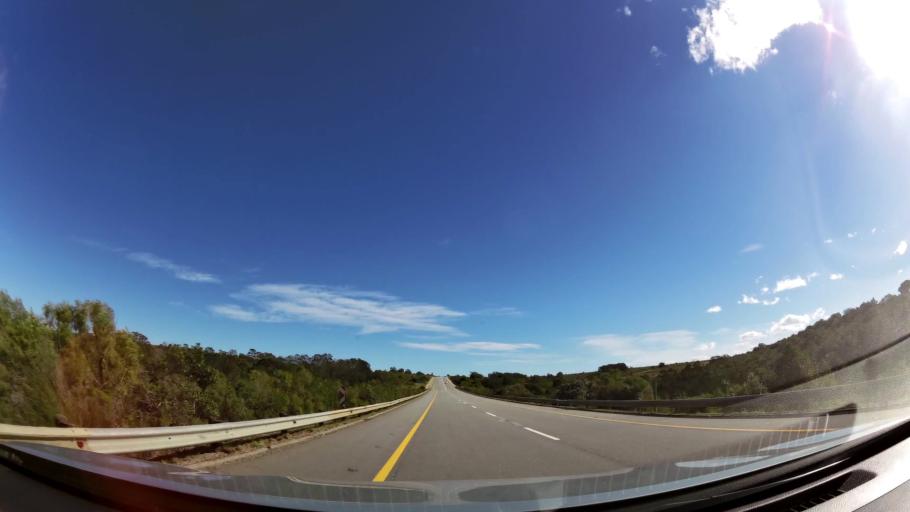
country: ZA
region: Eastern Cape
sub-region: Cacadu District Municipality
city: Kruisfontein
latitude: -34.0075
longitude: 24.6684
